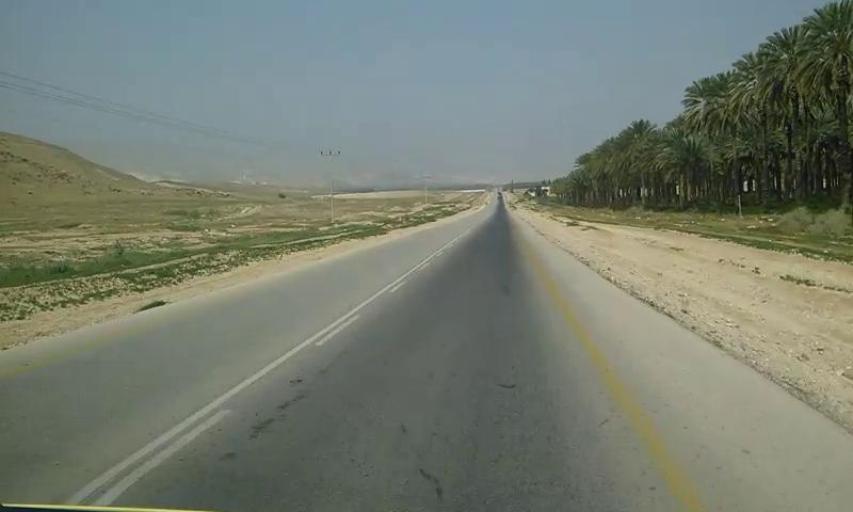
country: PS
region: West Bank
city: Al `Awja
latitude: 31.9794
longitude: 35.4663
